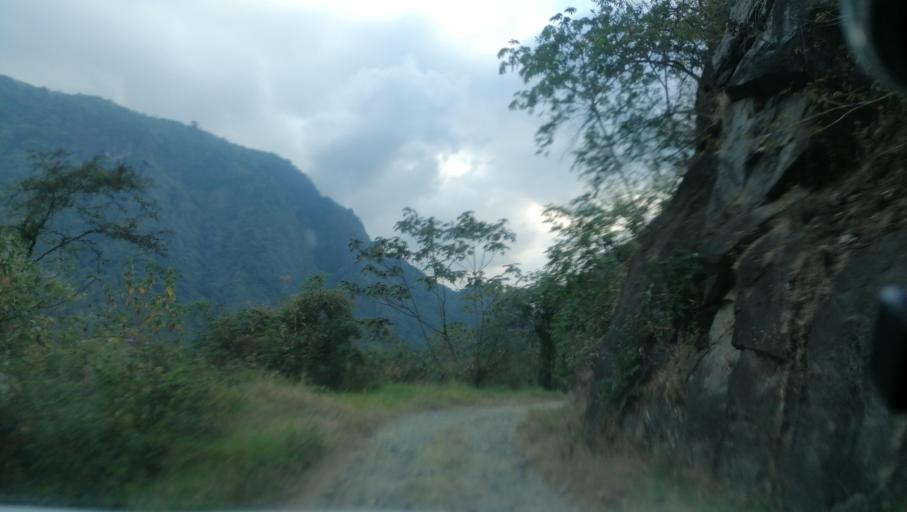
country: MX
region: Chiapas
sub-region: Cacahoatan
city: Benito Juarez
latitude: 15.1456
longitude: -92.1870
